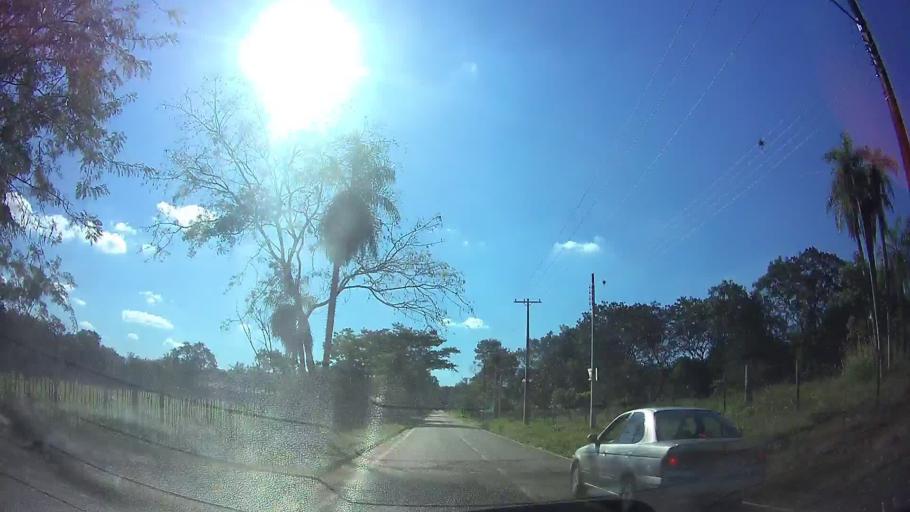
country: PY
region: Central
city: Limpio
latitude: -25.2100
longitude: -57.4789
